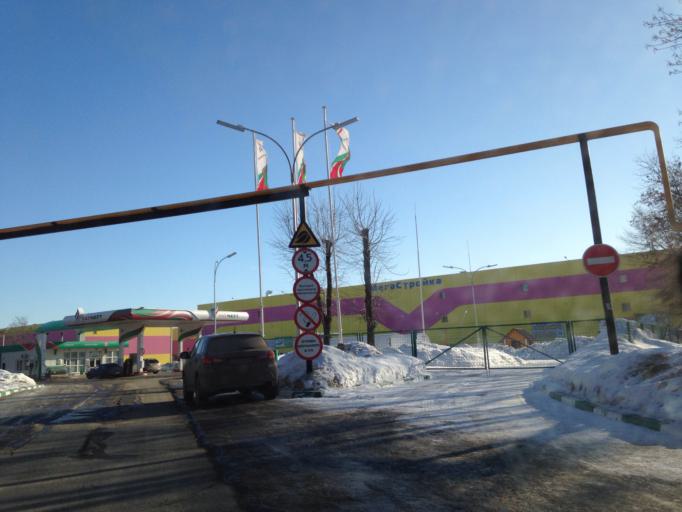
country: RU
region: Ulyanovsk
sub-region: Ulyanovskiy Rayon
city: Ulyanovsk
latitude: 54.2981
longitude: 48.3254
